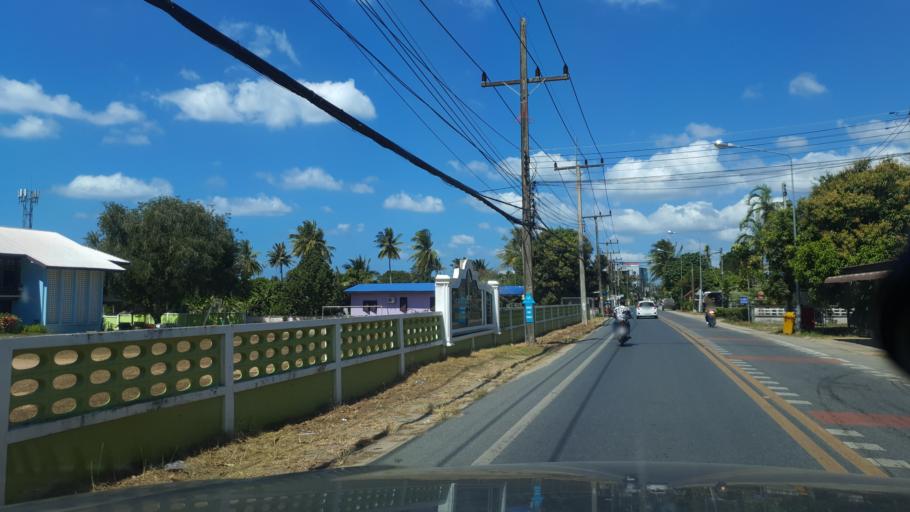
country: TH
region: Phuket
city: Thalang
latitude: 8.1317
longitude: 98.3075
